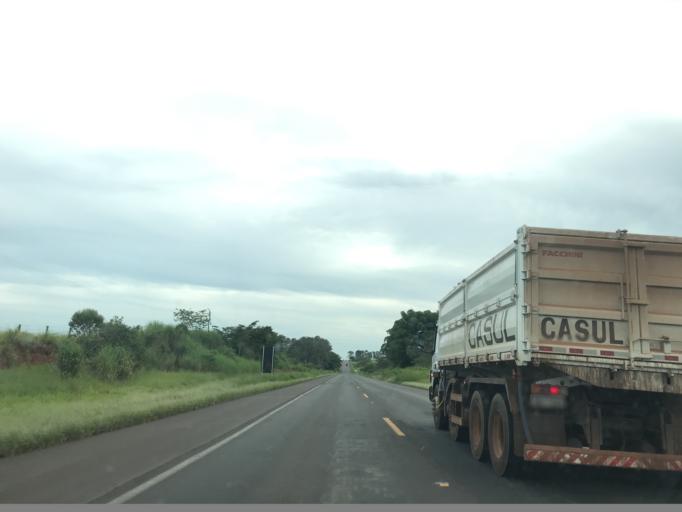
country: BR
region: Sao Paulo
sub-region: Tupa
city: Tupa
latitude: -21.6509
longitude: -50.5225
